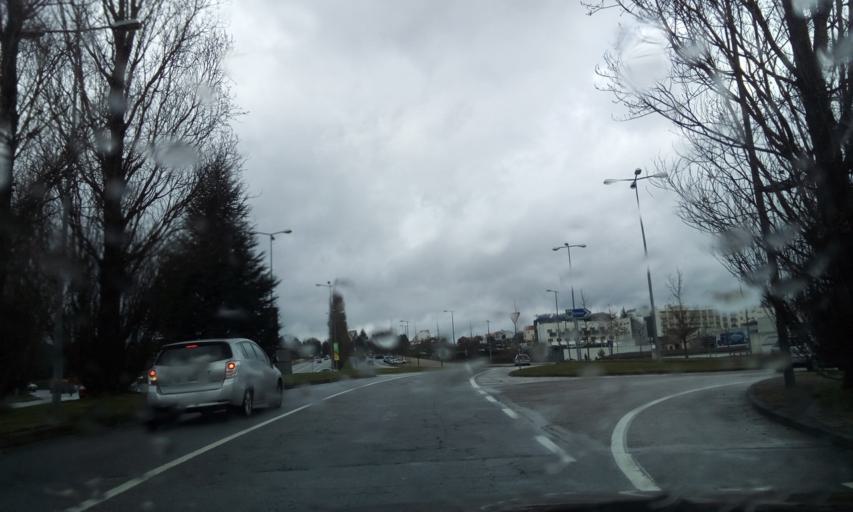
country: PT
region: Viseu
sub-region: Viseu
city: Abraveses
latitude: 40.6710
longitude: -7.9207
